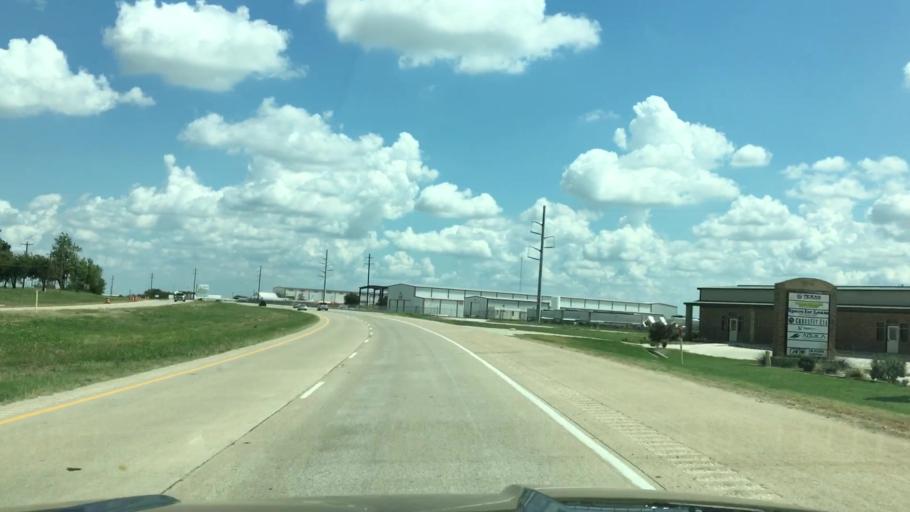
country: US
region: Texas
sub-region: Wise County
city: Rhome
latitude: 33.0378
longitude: -97.4422
